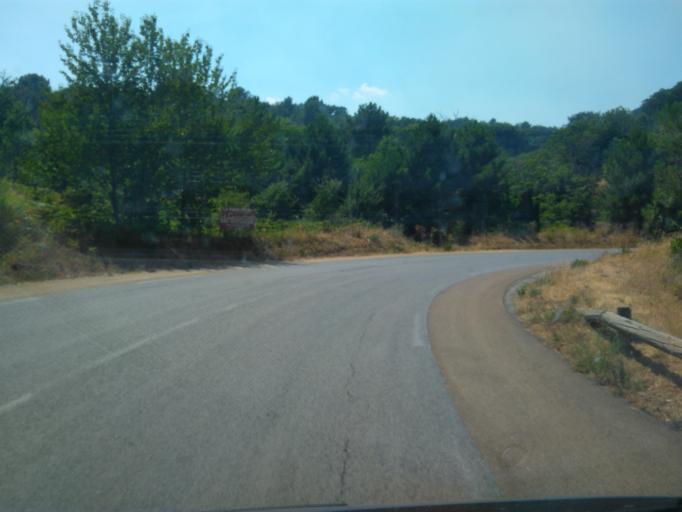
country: FR
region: Provence-Alpes-Cote d'Azur
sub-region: Departement du Var
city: La Garde-Freinet
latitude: 43.2991
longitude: 6.4756
